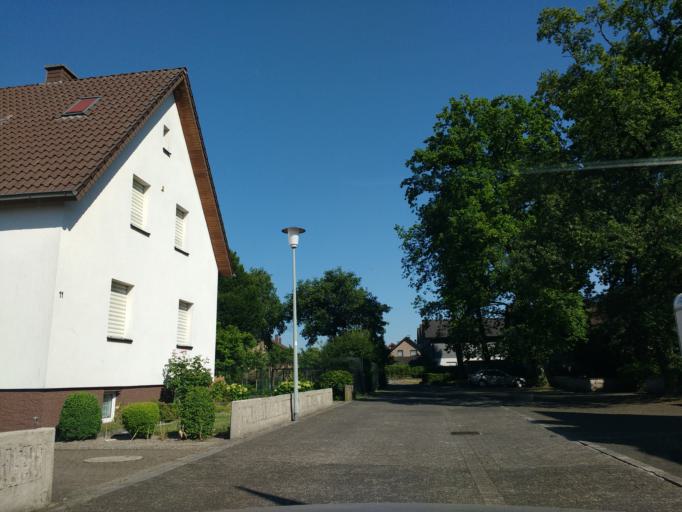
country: DE
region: North Rhine-Westphalia
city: Bad Lippspringe
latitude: 51.7595
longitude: 8.7781
